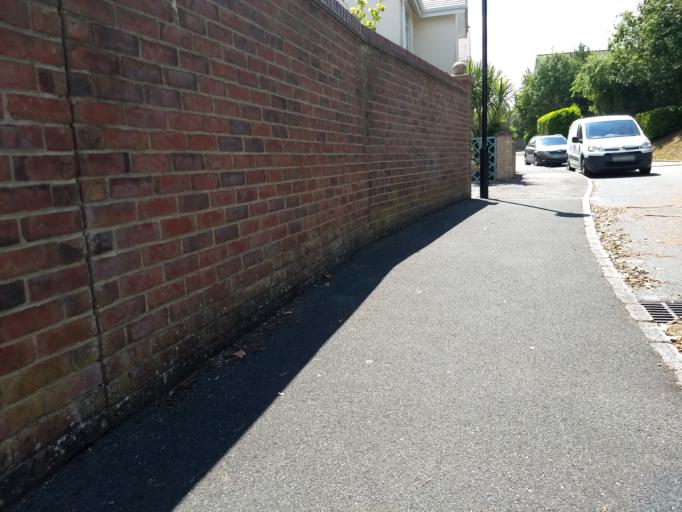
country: GB
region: England
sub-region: Isle of Wight
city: Ryde
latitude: 50.7135
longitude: -1.1438
